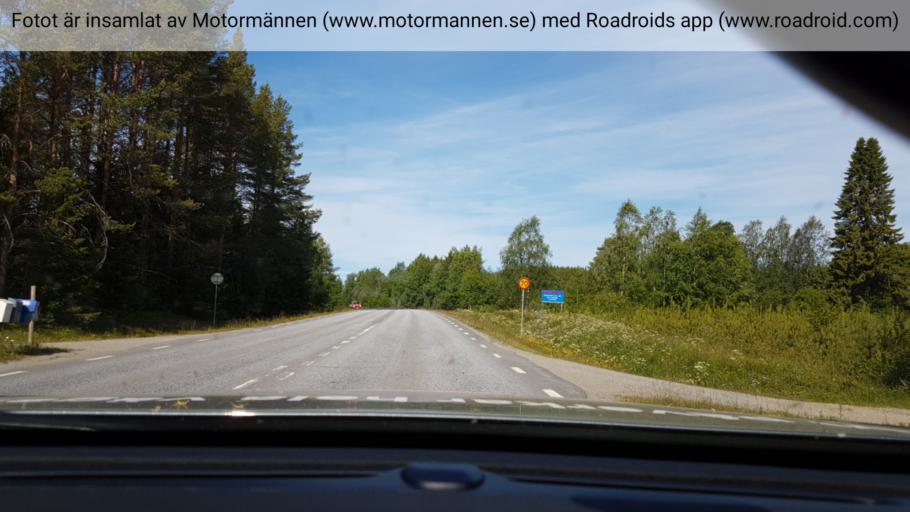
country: SE
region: Vaesterbotten
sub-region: Dorotea Kommun
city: Dorotea
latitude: 64.2546
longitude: 16.4568
